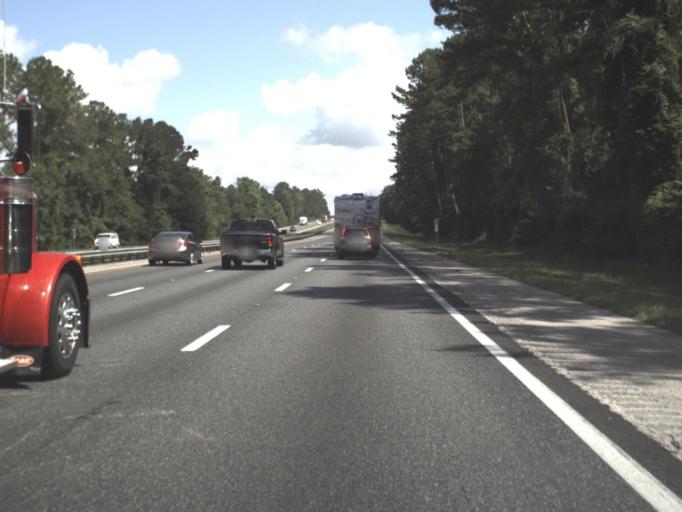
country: US
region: Florida
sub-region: Alachua County
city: Alachua
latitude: 29.7264
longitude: -82.4712
